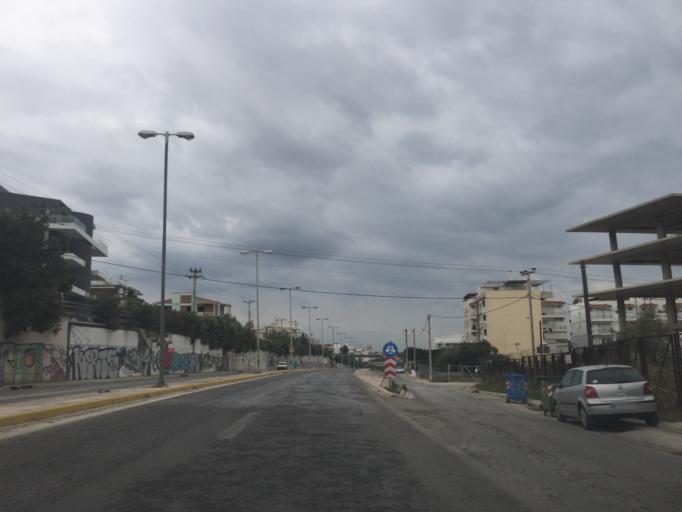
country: GR
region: Attica
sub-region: Nomarchia Anatolikis Attikis
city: Voula
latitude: 37.8410
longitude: 23.7720
